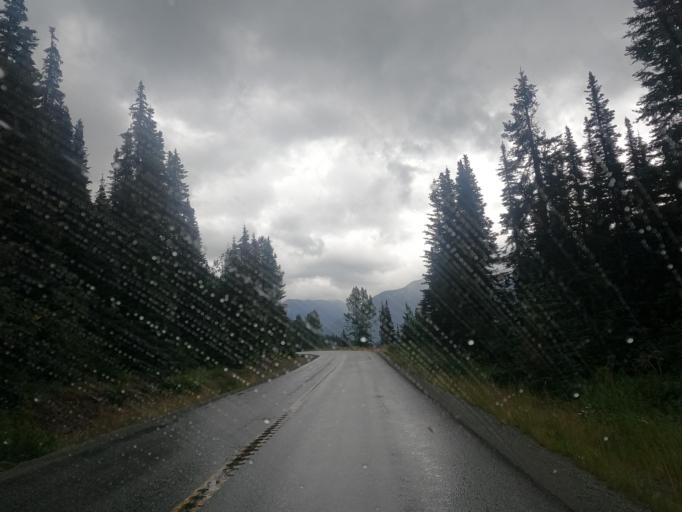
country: CA
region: British Columbia
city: Pemberton
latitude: 50.3843
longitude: -122.4343
